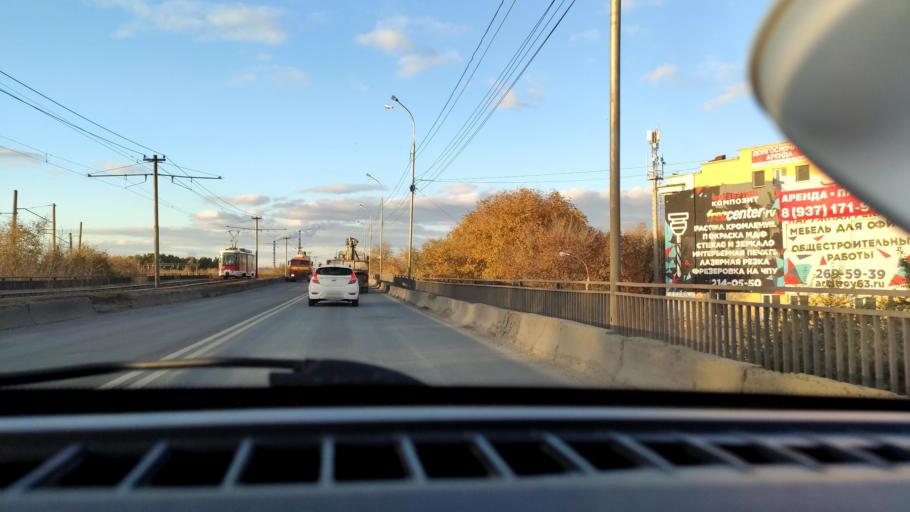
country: RU
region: Samara
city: Smyshlyayevka
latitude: 53.2188
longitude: 50.2904
